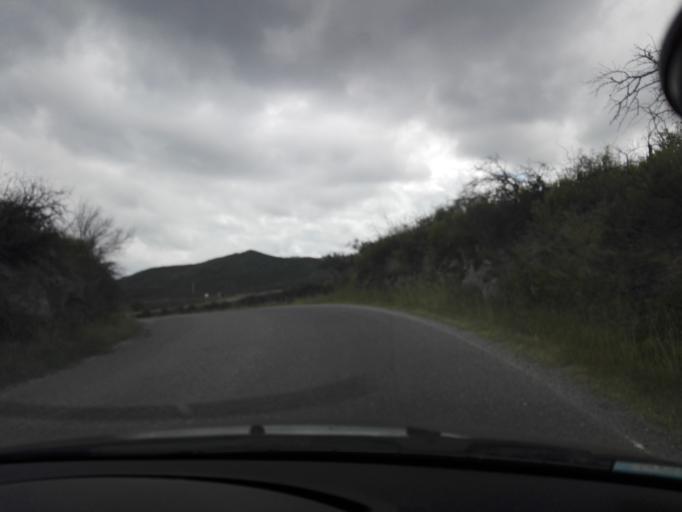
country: AR
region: Cordoba
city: Alta Gracia
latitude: -31.5905
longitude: -64.5091
